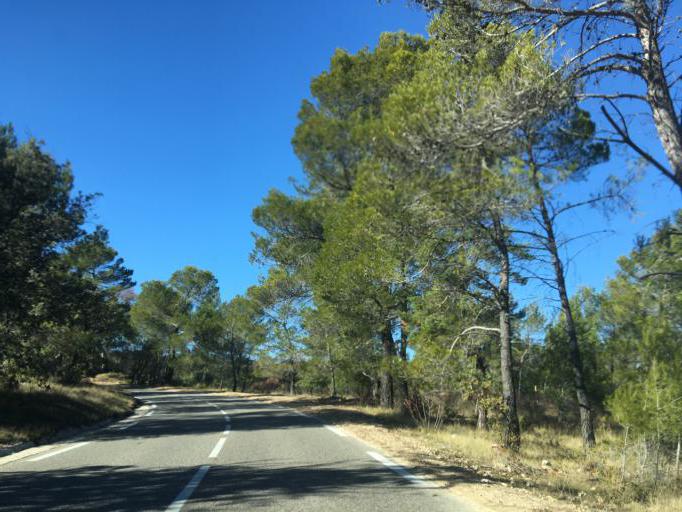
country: FR
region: Provence-Alpes-Cote d'Azur
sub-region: Departement du Var
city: Barjols
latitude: 43.5969
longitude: 5.9861
